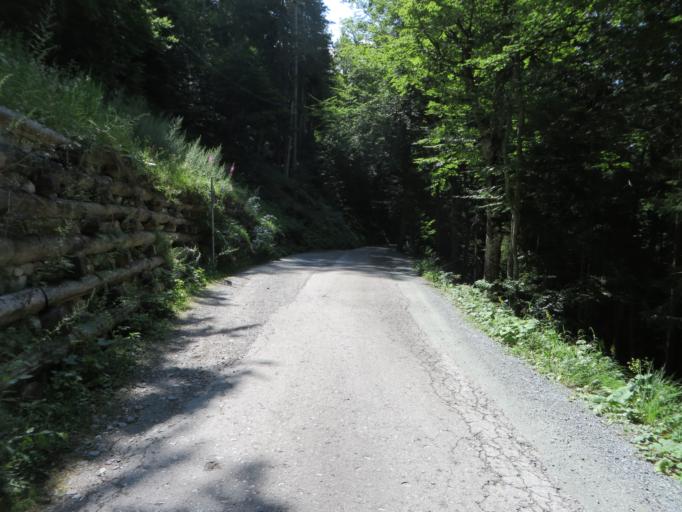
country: IT
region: Trentino-Alto Adige
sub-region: Provincia di Trento
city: Carisolo
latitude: 46.2116
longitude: 10.8297
